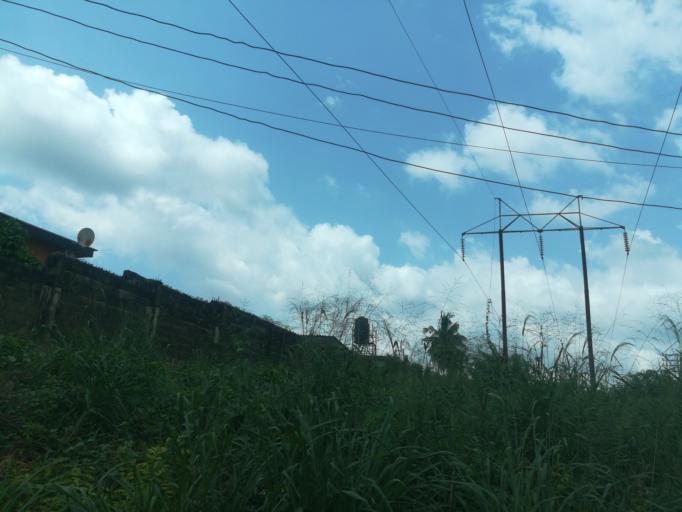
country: NG
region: Oyo
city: Ibadan
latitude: 7.3639
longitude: 3.8586
